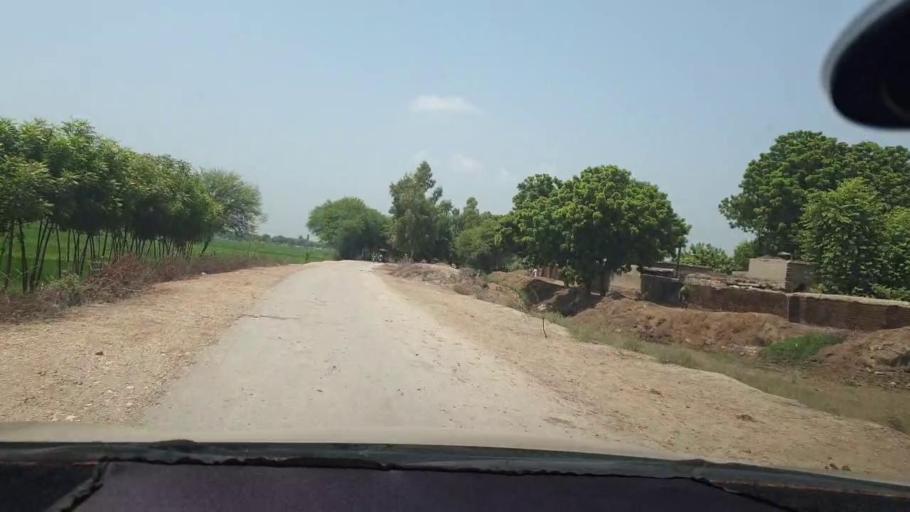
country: PK
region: Sindh
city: Kambar
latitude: 27.6631
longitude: 67.9282
